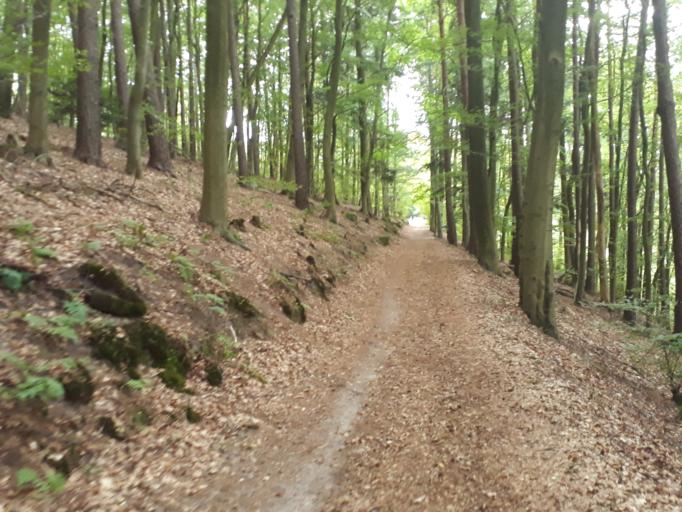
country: DE
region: Rheinland-Pfalz
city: Kaiserslautern
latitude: 49.4162
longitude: 7.7813
